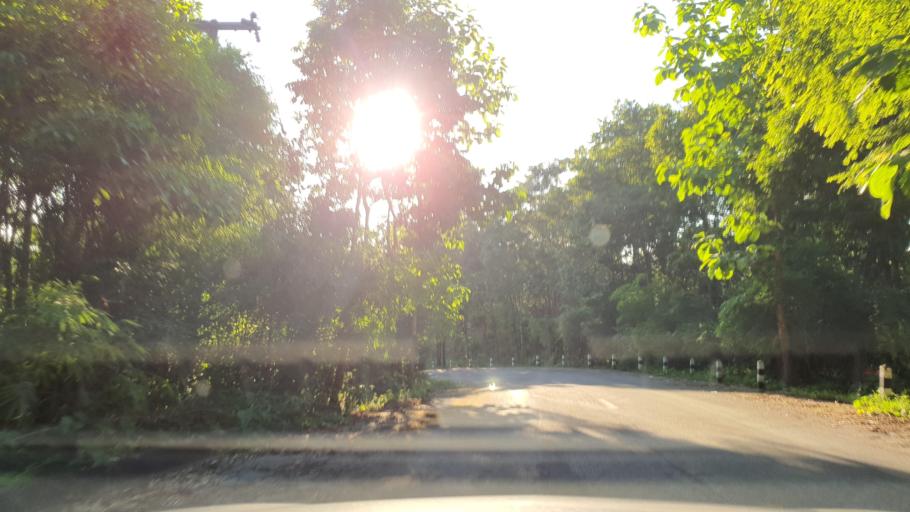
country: TH
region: Chiang Mai
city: Mae On
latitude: 18.8259
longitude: 99.2938
